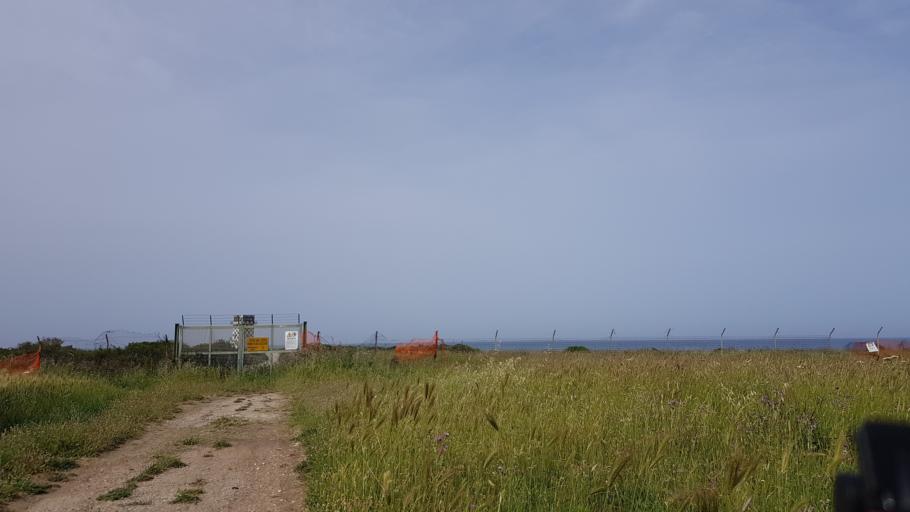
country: IT
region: Apulia
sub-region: Provincia di Brindisi
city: La Rosa
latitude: 40.5911
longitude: 18.0406
